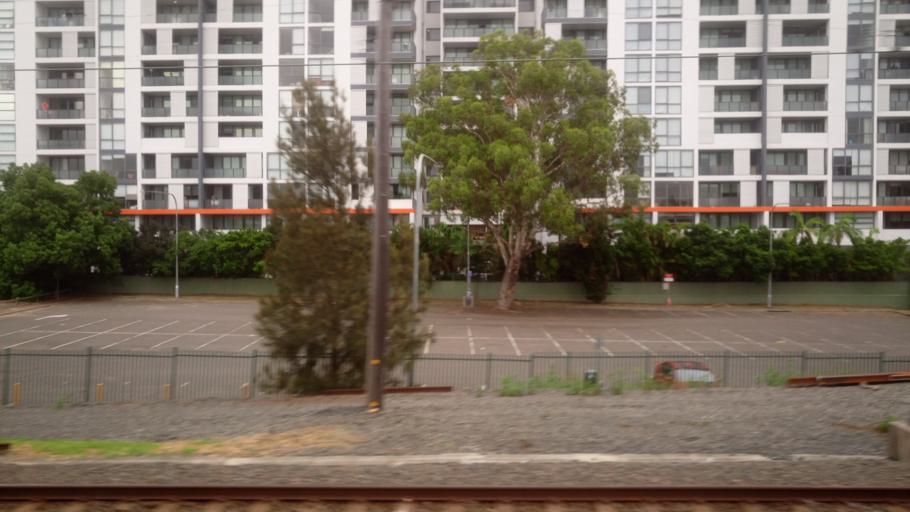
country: AU
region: New South Wales
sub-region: Parramatta
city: Harris Park
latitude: -33.8215
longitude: 151.0078
